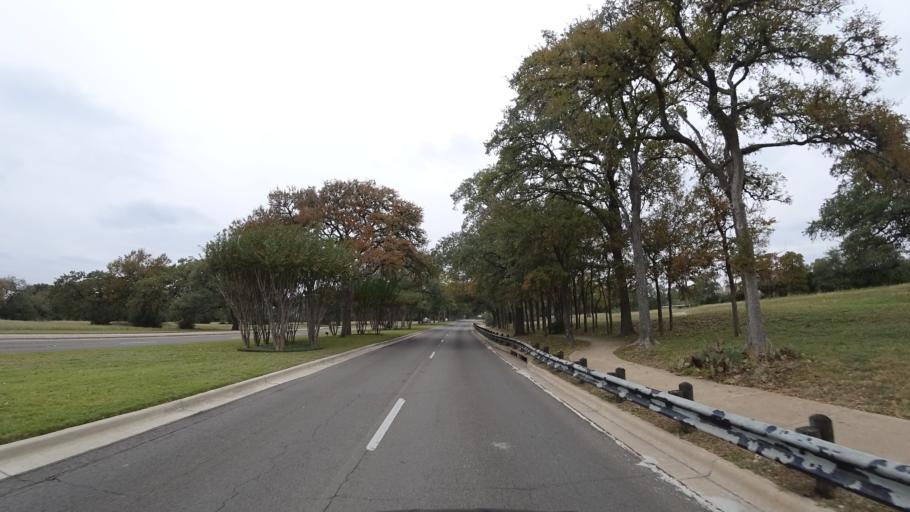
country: US
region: Texas
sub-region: Travis County
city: Shady Hollow
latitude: 30.2018
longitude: -97.8818
